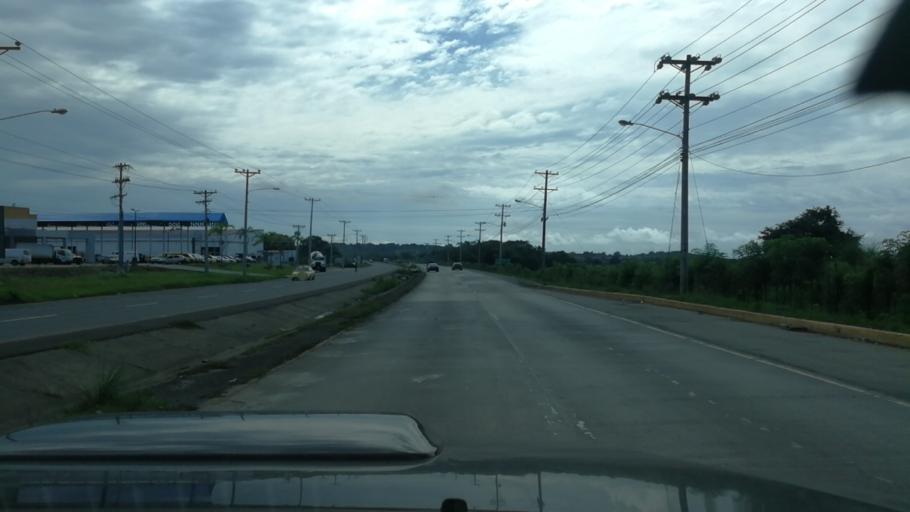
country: PA
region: Panama
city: Pacora
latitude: 9.0981
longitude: -79.2866
